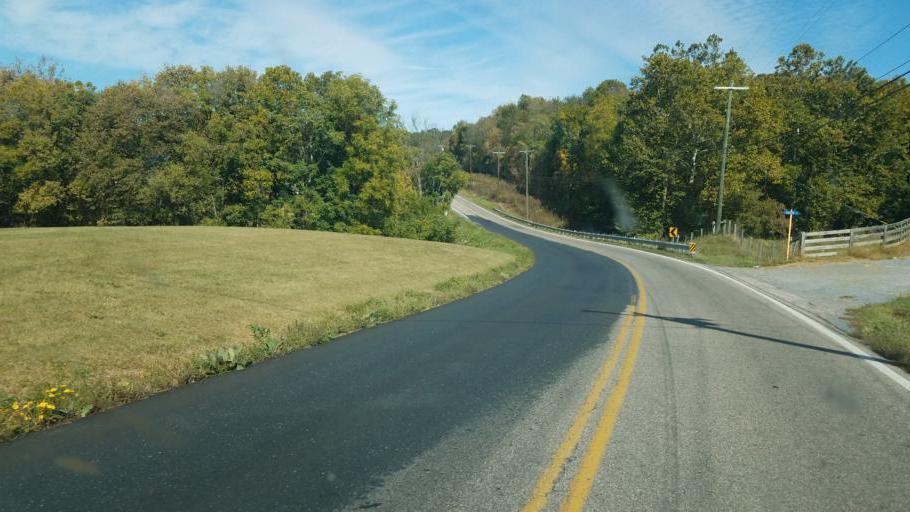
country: US
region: Virginia
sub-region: Page County
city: Shenandoah
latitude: 38.5132
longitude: -78.6193
